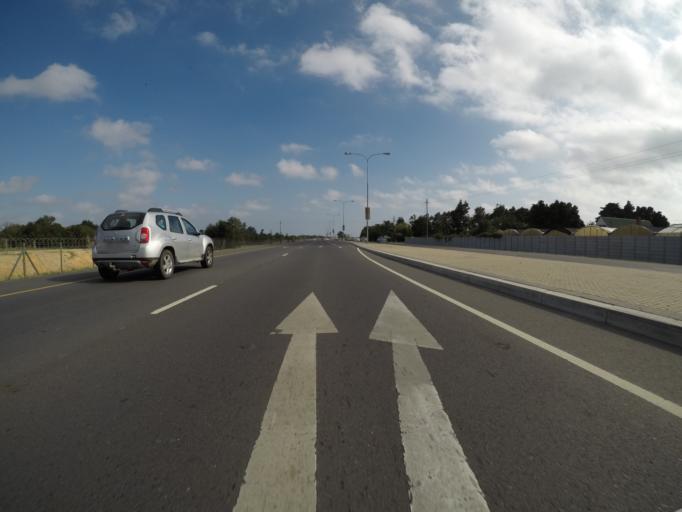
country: ZA
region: Western Cape
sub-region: Cape Winelands District Municipality
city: Stellenbosch
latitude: -33.9930
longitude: 18.7647
